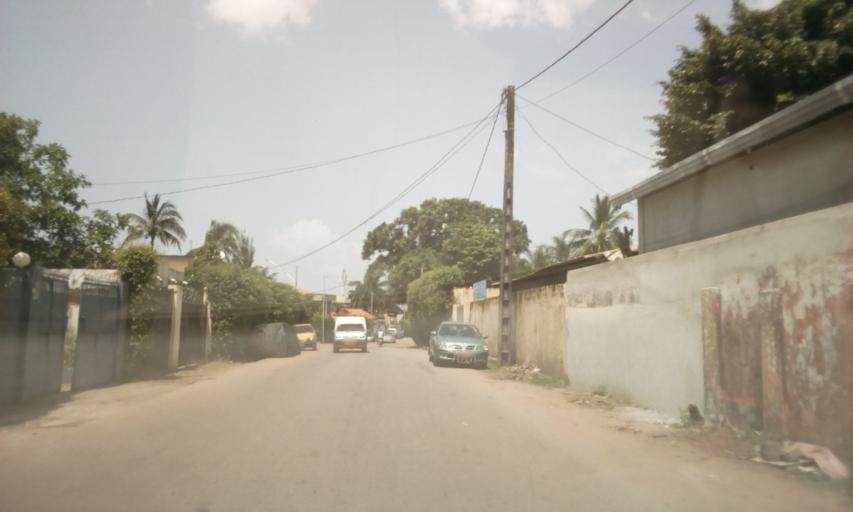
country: GN
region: Conakry
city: Conakry
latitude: 9.5666
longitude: -13.6621
